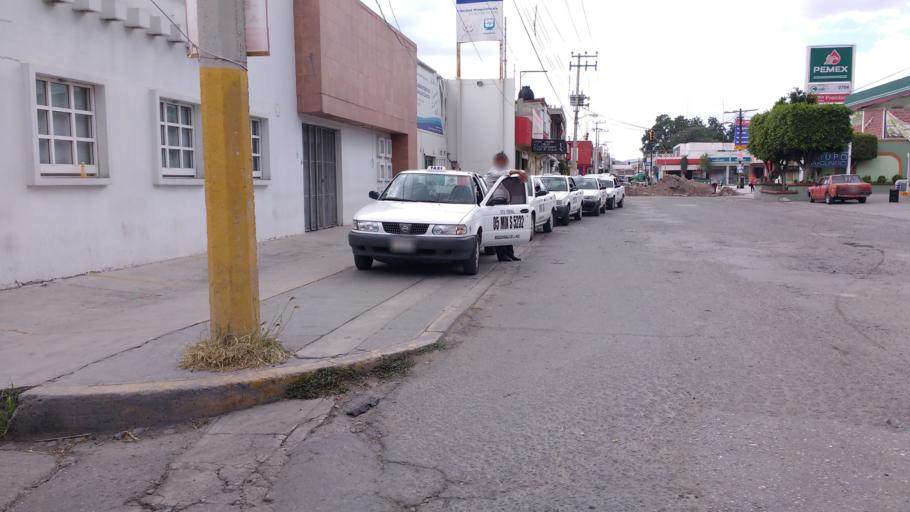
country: MX
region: Hidalgo
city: Mixquiahuala de Juarez
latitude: 20.2269
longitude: -99.2160
